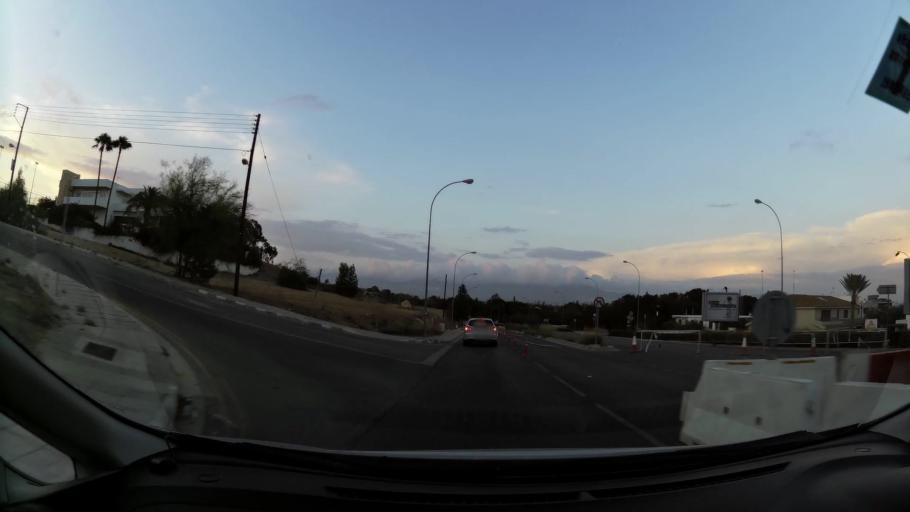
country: CY
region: Lefkosia
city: Nicosia
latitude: 35.1541
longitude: 33.3823
